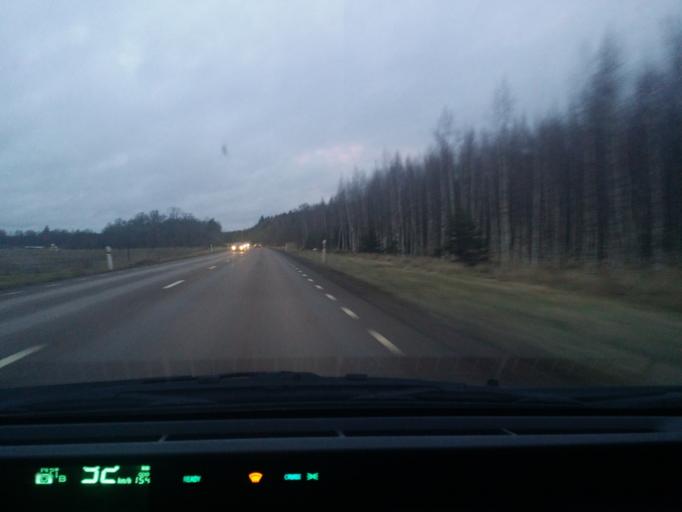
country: SE
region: Soedermanland
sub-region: Eskilstuna Kommun
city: Kvicksund
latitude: 59.4850
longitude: 16.3055
